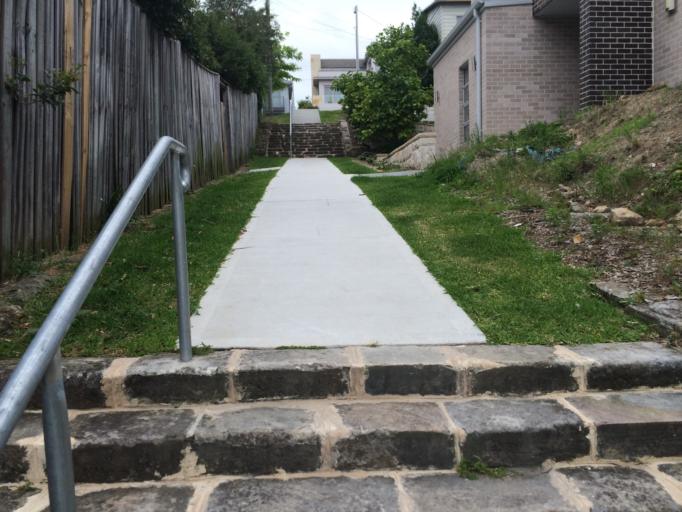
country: AU
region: New South Wales
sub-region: Hunters Hill
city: Gladesville
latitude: -33.8316
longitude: 151.1204
